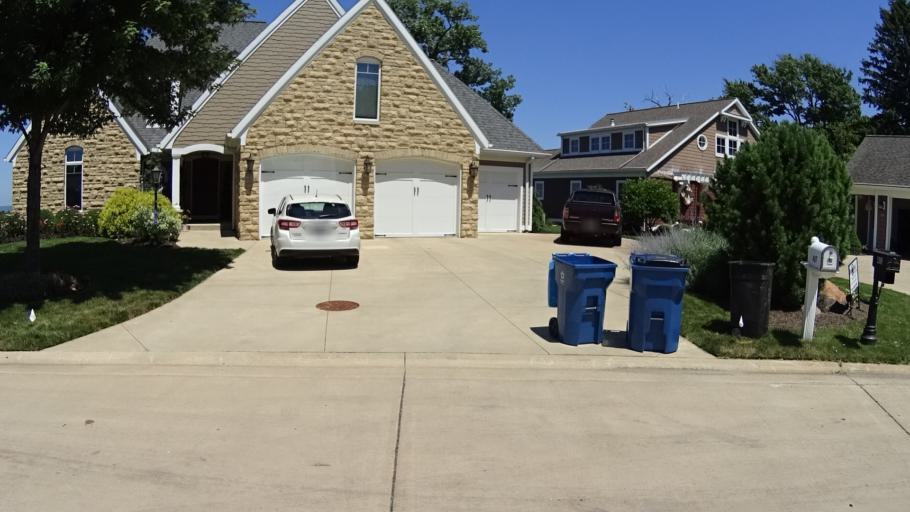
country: US
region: Ohio
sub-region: Erie County
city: Huron
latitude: 41.3986
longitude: -82.5560
